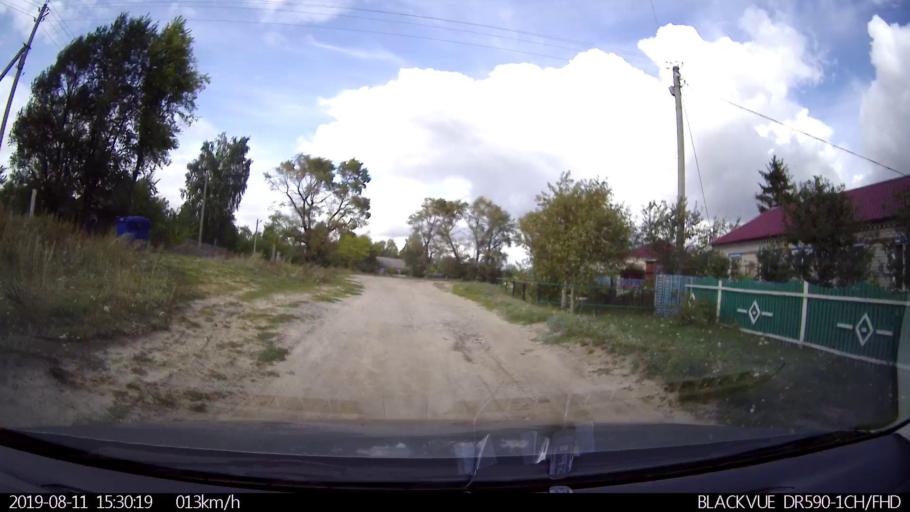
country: RU
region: Ulyanovsk
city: Ignatovka
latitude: 53.8557
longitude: 47.5749
